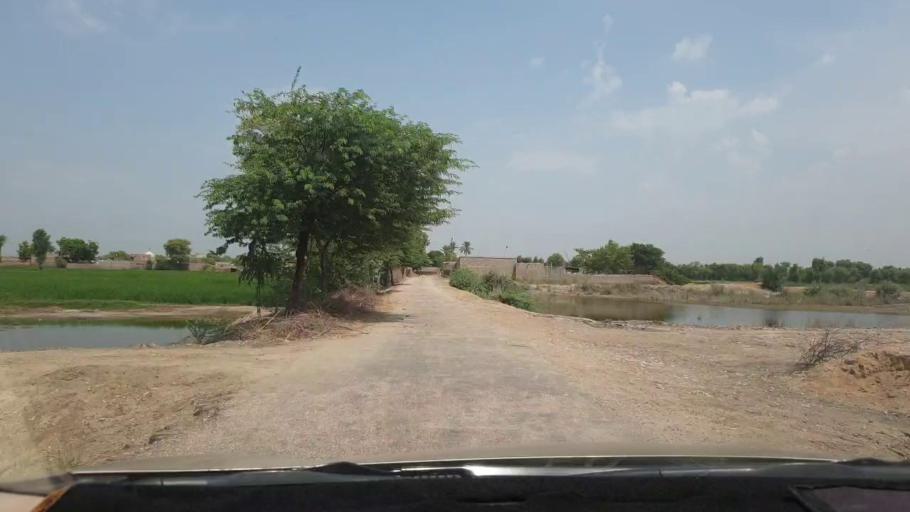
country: PK
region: Sindh
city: Naudero
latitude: 27.7387
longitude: 68.3668
